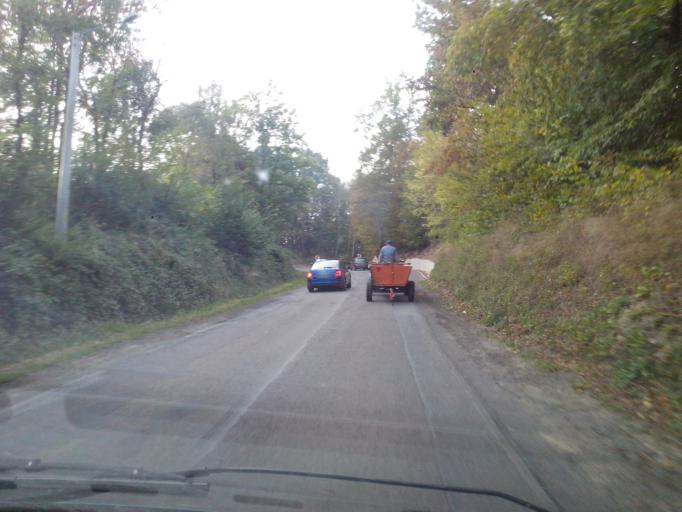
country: PL
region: Subcarpathian Voivodeship
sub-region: Powiat strzyzowski
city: Jawornik
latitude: 49.8175
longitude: 21.8393
